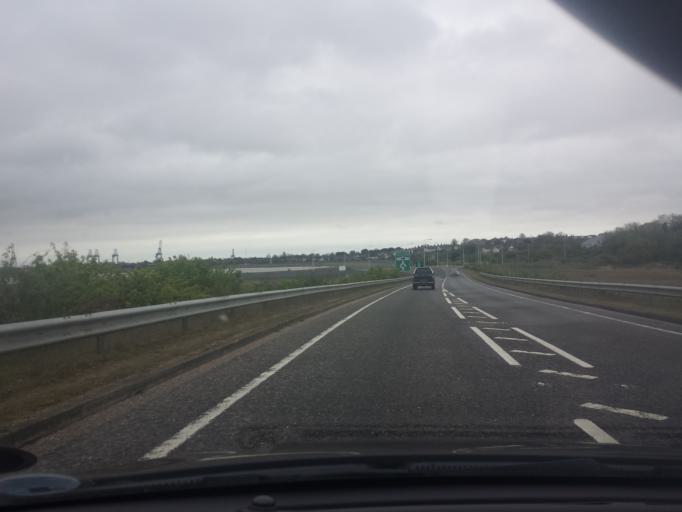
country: GB
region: England
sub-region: Essex
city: Dovercourt
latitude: 51.9400
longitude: 1.2674
